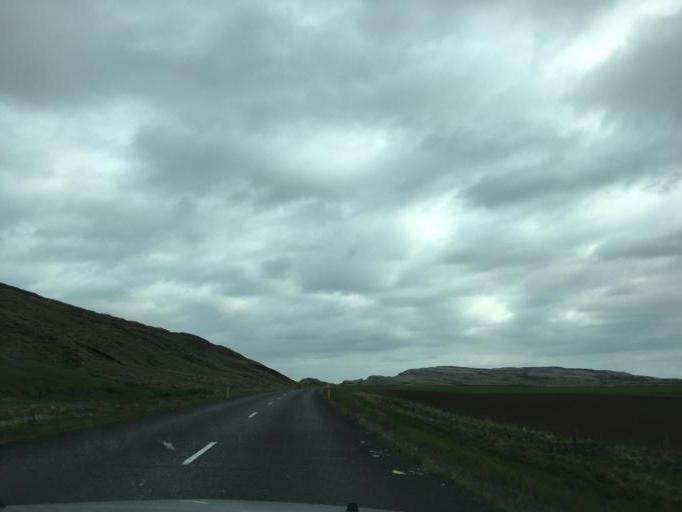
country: IS
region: South
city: Vestmannaeyjar
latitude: 64.2172
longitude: -20.2615
